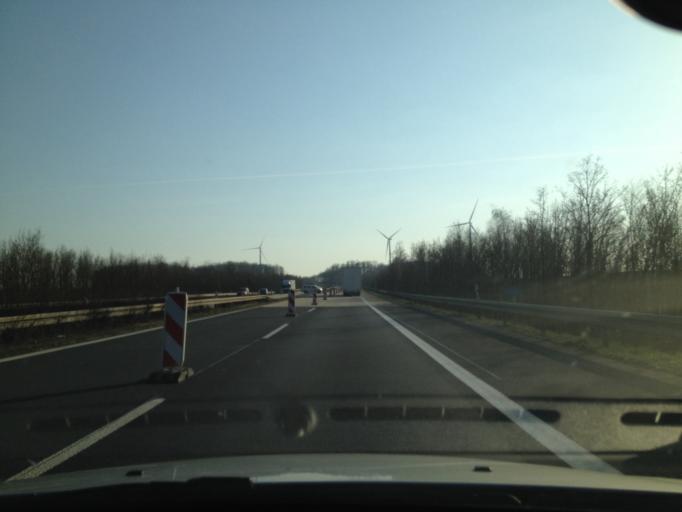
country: DE
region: Bavaria
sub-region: Regierungsbezirk Mittelfranken
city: Gollhofen
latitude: 49.5635
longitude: 10.1688
